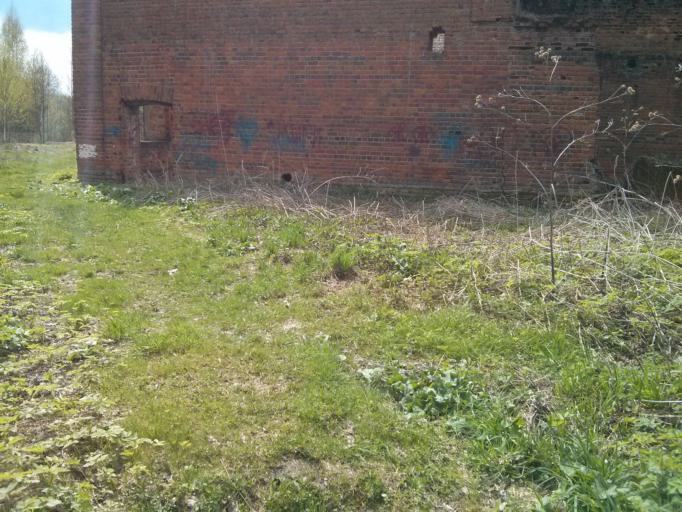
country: RU
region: Nizjnij Novgorod
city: Shimorskoye
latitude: 55.3089
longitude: 41.8522
